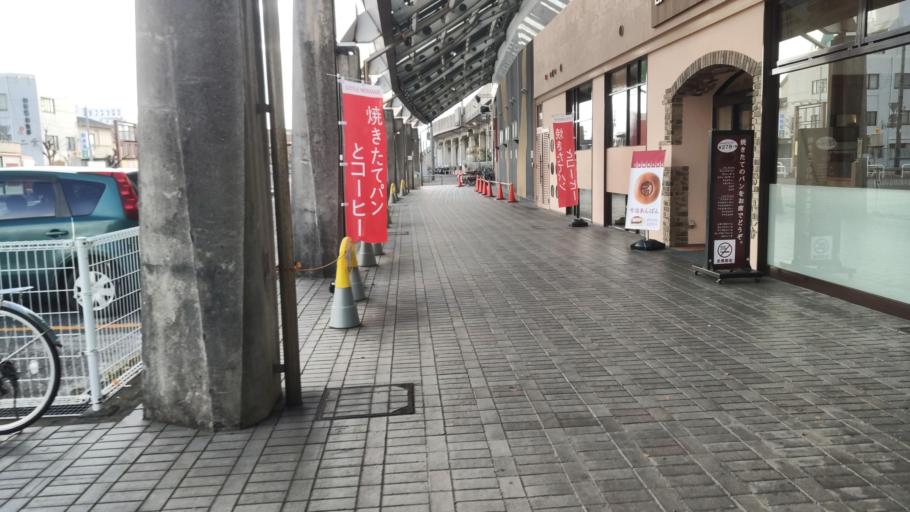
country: JP
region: Ehime
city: Hojo
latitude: 34.0643
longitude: 132.9940
